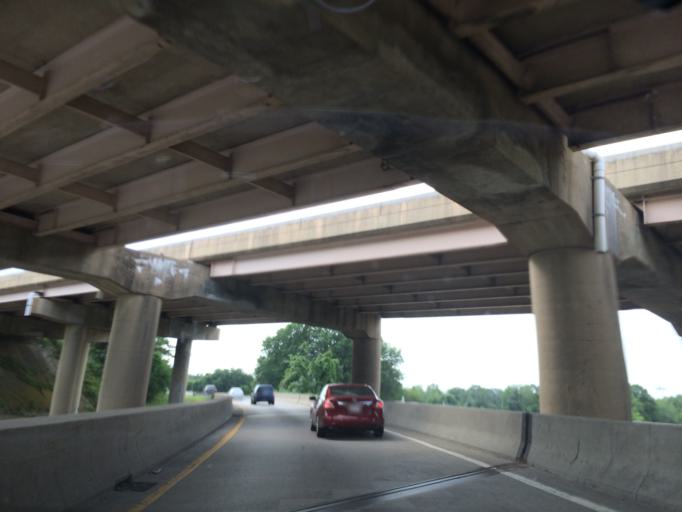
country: US
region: Maryland
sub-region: Baltimore County
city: Woodlawn
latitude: 39.3056
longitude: -76.7437
